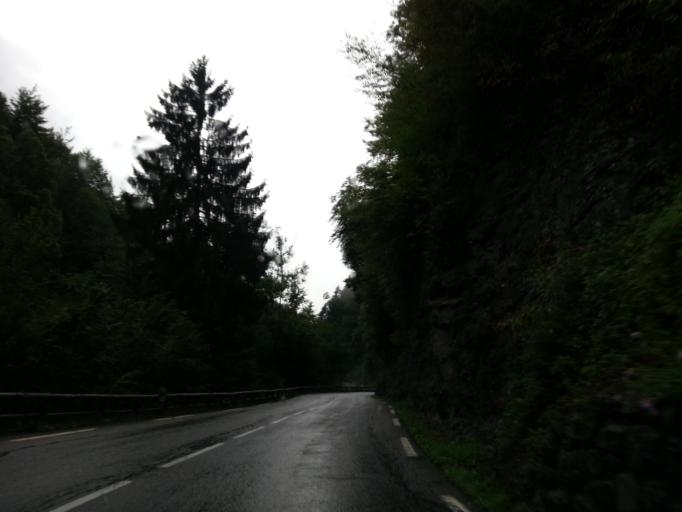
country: FR
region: Rhone-Alpes
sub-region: Departement de la Savoie
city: Marthod
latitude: 45.7089
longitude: 6.4359
